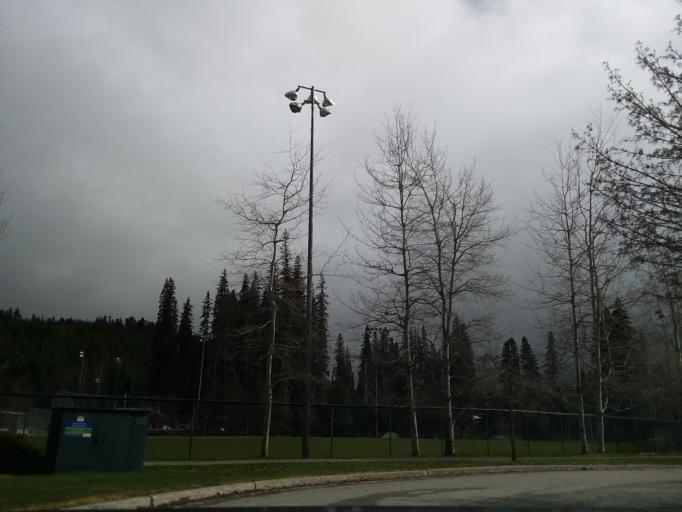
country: CA
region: British Columbia
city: Whistler
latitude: 50.1334
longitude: -122.9494
